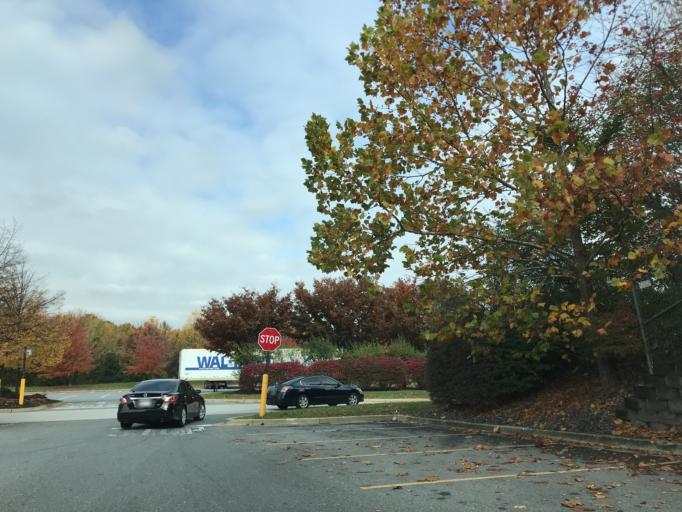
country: US
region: Maryland
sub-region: Baltimore County
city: Overlea
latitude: 39.3784
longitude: -76.5072
